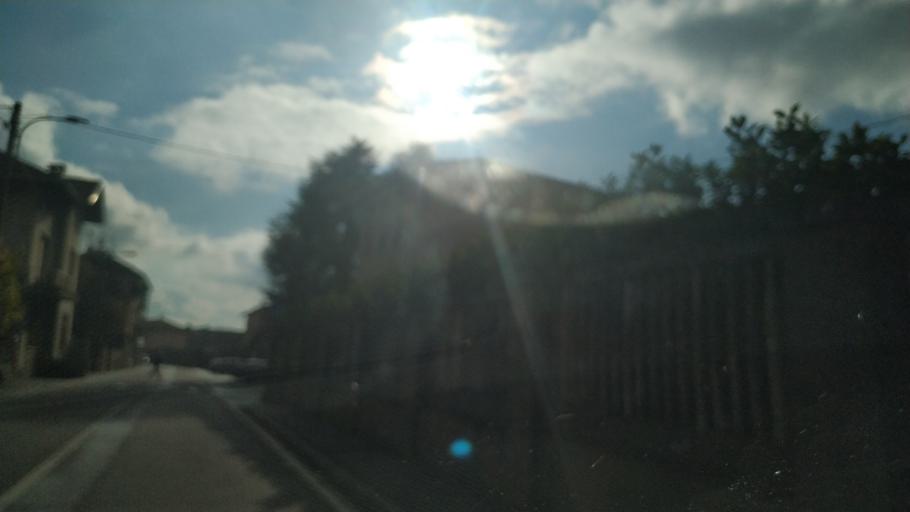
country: IT
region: Piedmont
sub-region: Provincia di Biella
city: Ponderano
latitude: 45.5400
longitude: 8.0541
